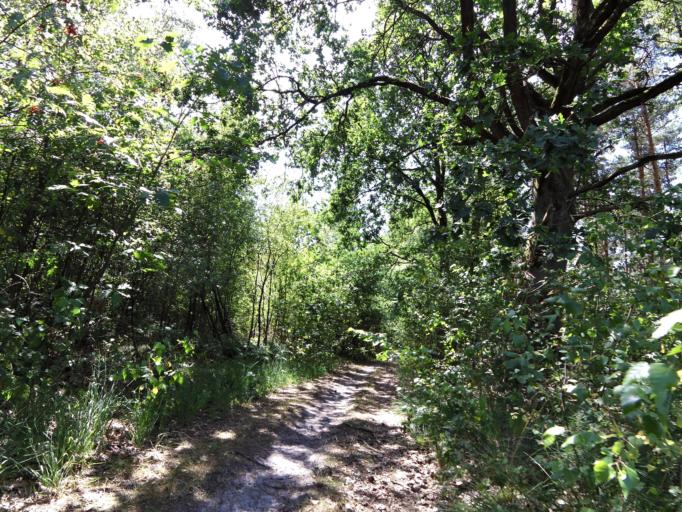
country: NL
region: Limburg
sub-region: Gemeente Leudal
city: Heythuysen
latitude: 51.2088
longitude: 5.8963
